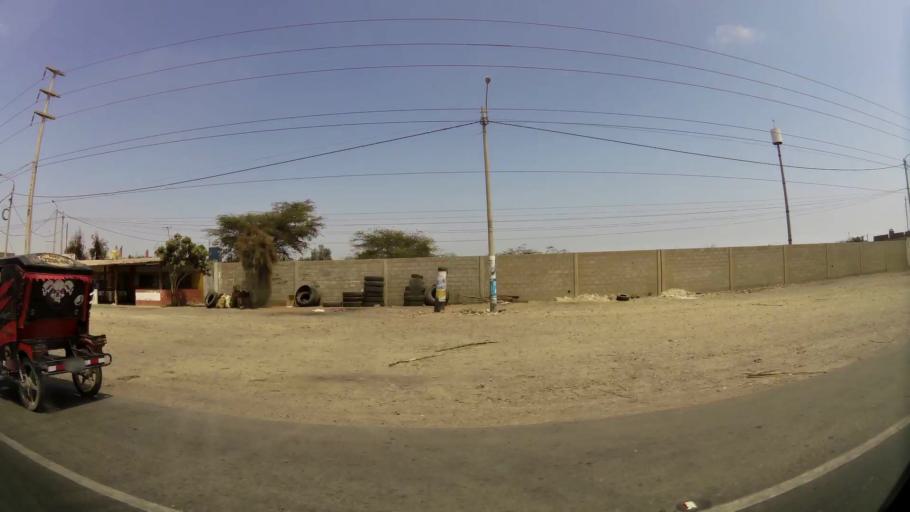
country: PE
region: La Libertad
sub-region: Provincia de Pacasmayo
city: Pacasmayo
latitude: -7.4136
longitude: -79.5510
